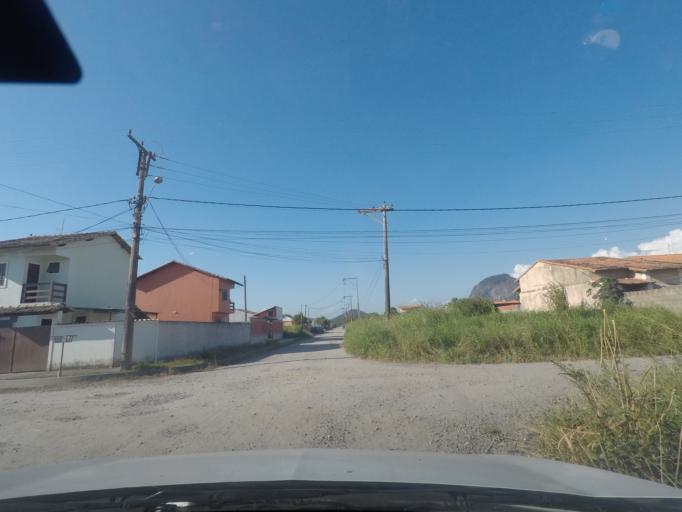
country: BR
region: Rio de Janeiro
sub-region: Marica
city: Marica
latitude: -22.9645
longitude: -42.9307
